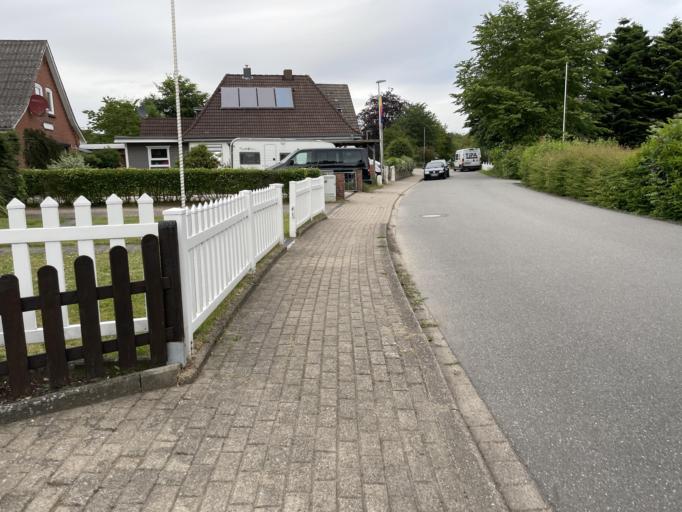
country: DE
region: Schleswig-Holstein
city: Mildstedt
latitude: 54.4594
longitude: 9.0918
